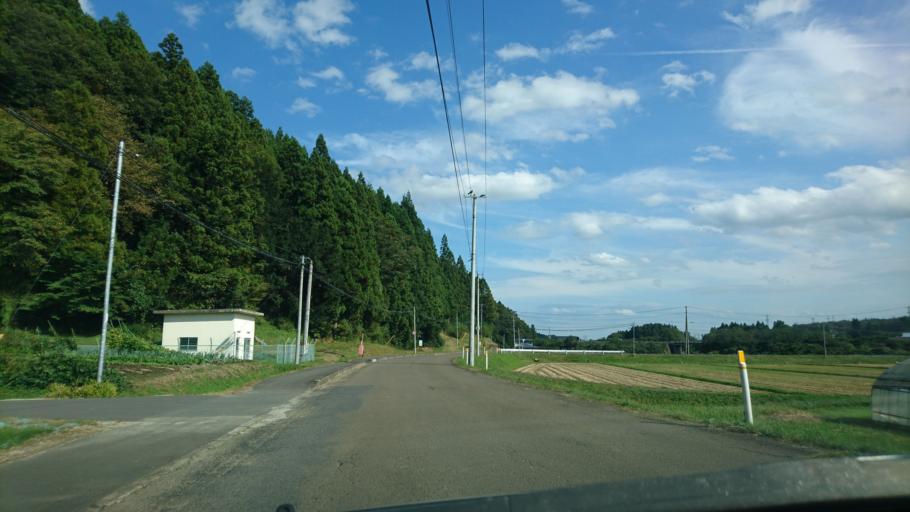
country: JP
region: Iwate
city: Ichinoseki
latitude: 38.8721
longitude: 141.1104
